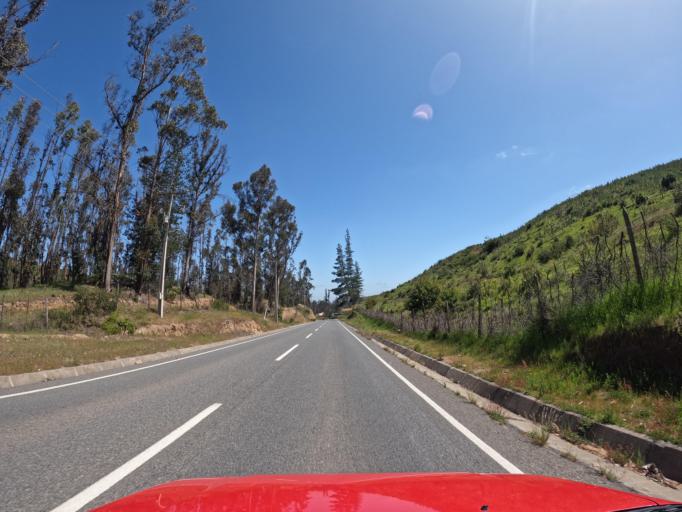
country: CL
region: O'Higgins
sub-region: Provincia de Colchagua
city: Santa Cruz
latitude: -34.6787
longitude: -71.7948
